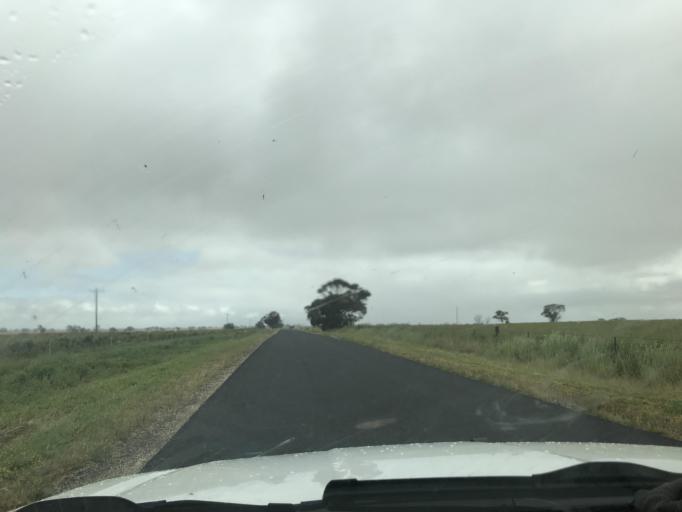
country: AU
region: South Australia
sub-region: Tatiara
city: Bordertown
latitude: -36.2954
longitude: 141.1461
